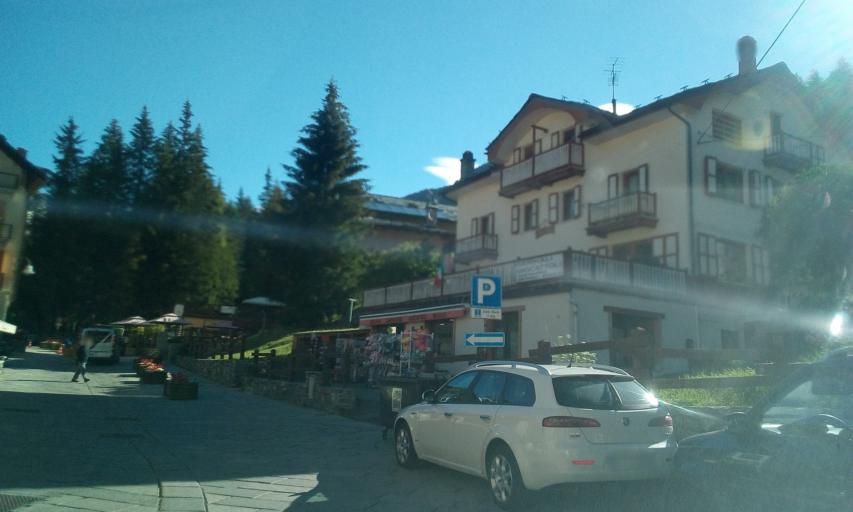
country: IT
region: Aosta Valley
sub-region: Valle d'Aosta
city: Antagnod
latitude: 45.8319
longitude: 7.7266
